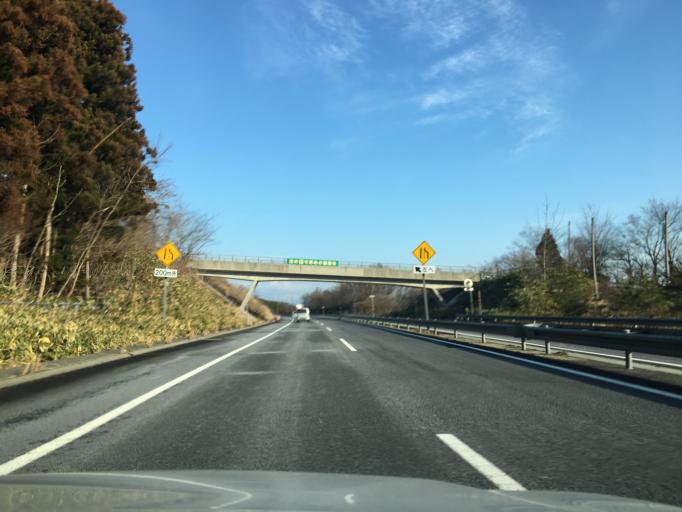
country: JP
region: Yamagata
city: Sagae
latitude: 38.4223
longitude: 140.1719
